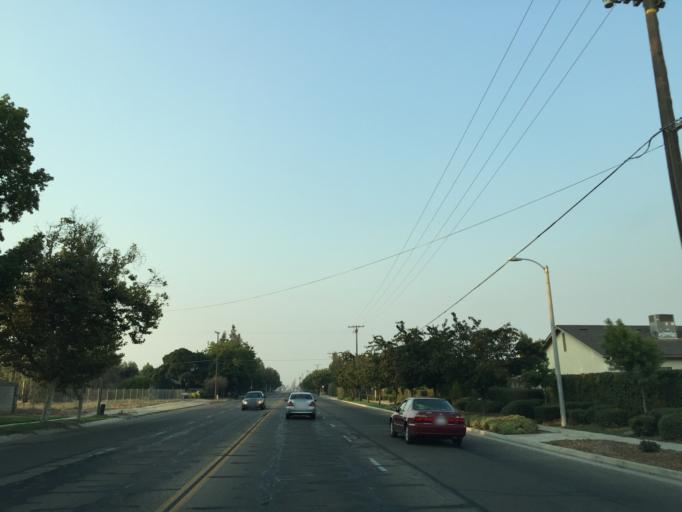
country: US
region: California
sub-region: Tulare County
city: Visalia
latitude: 36.3487
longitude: -119.2789
